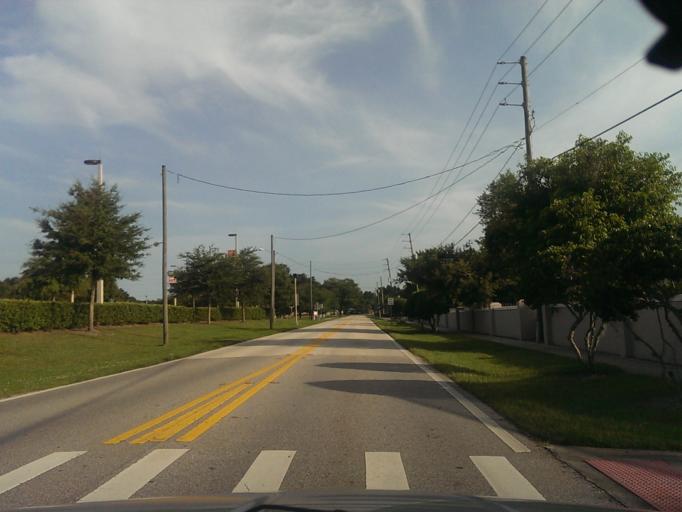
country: US
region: Florida
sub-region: Orange County
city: Winter Garden
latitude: 28.5406
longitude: -81.5693
